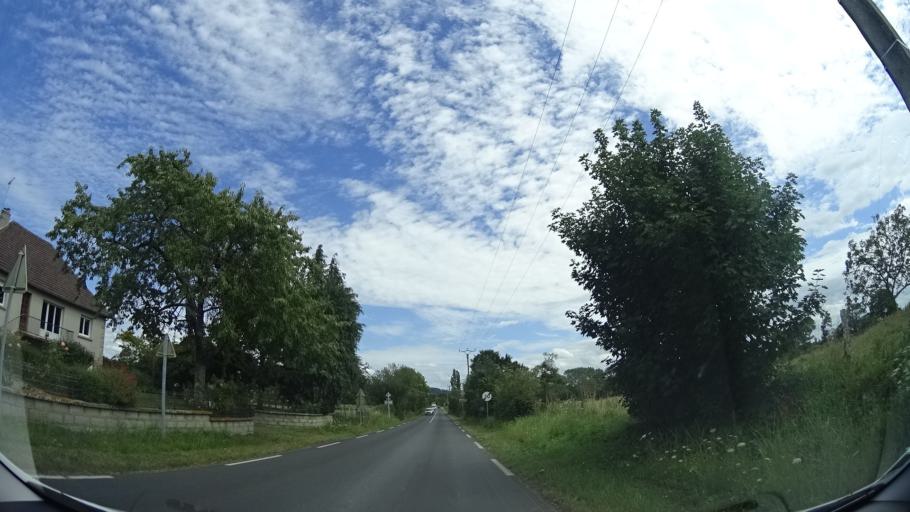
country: FR
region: Lower Normandy
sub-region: Departement de la Manche
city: Marcey-les-Greves
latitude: 48.6813
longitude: -1.4113
